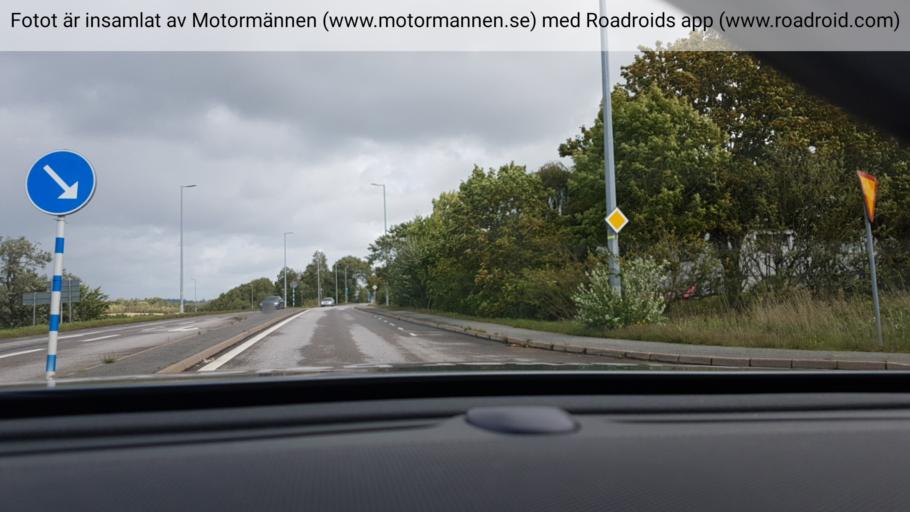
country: SE
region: Vaestra Goetaland
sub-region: Partille Kommun
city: Partille
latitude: 57.7962
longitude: 12.1398
